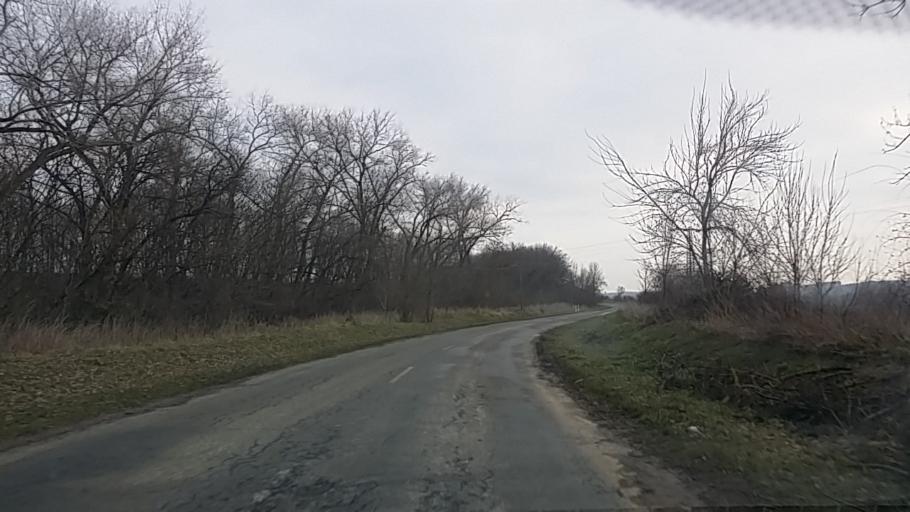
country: HU
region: Baranya
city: Lanycsok
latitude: 46.1027
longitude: 18.5438
